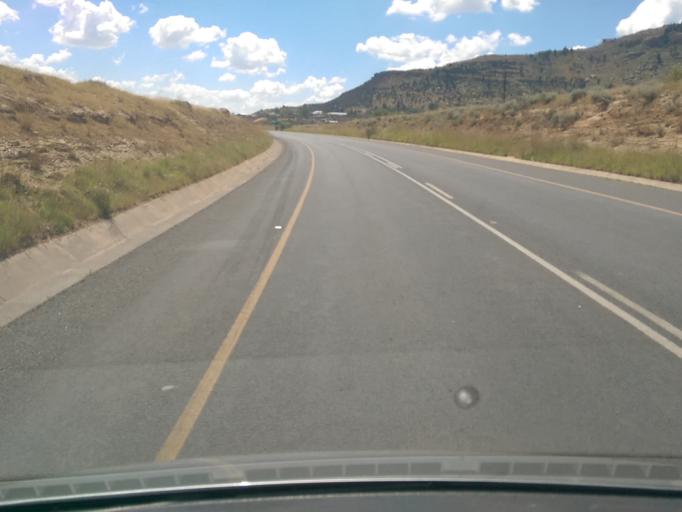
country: LS
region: Maseru
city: Maseru
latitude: -29.3686
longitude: 27.4738
